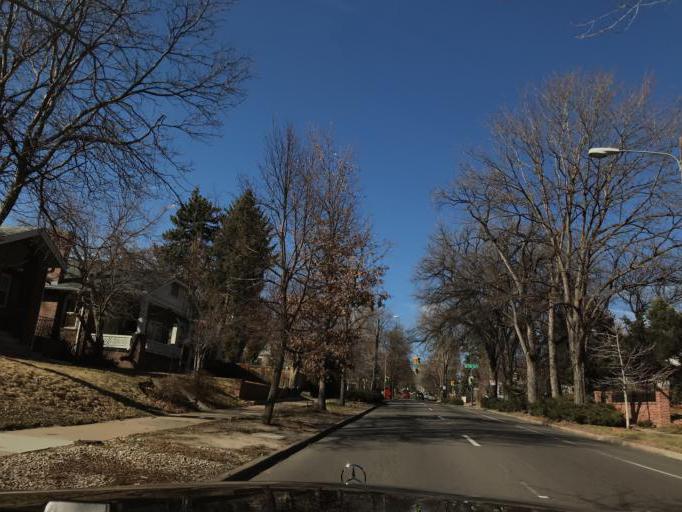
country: US
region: Colorado
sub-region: Denver County
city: Denver
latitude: 39.7264
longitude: -104.9591
